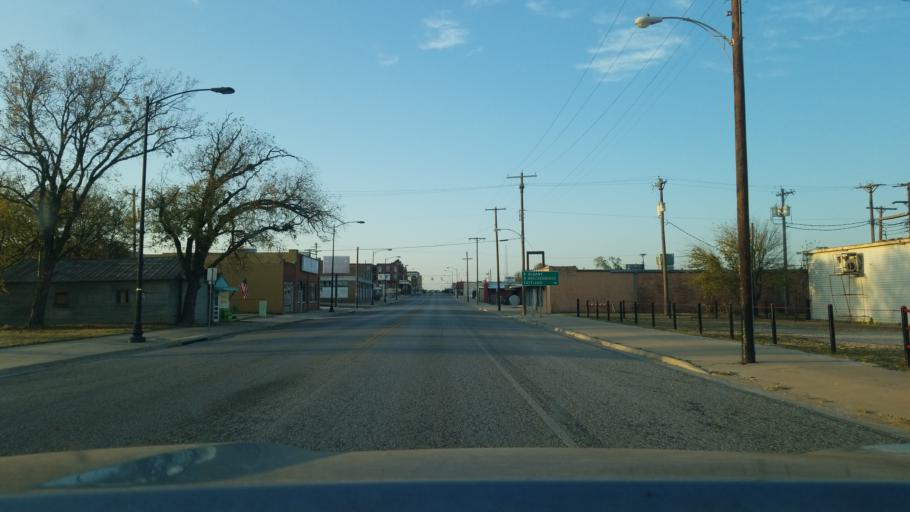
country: US
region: Texas
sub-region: Eastland County
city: Cisco
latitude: 32.3857
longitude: -98.9777
